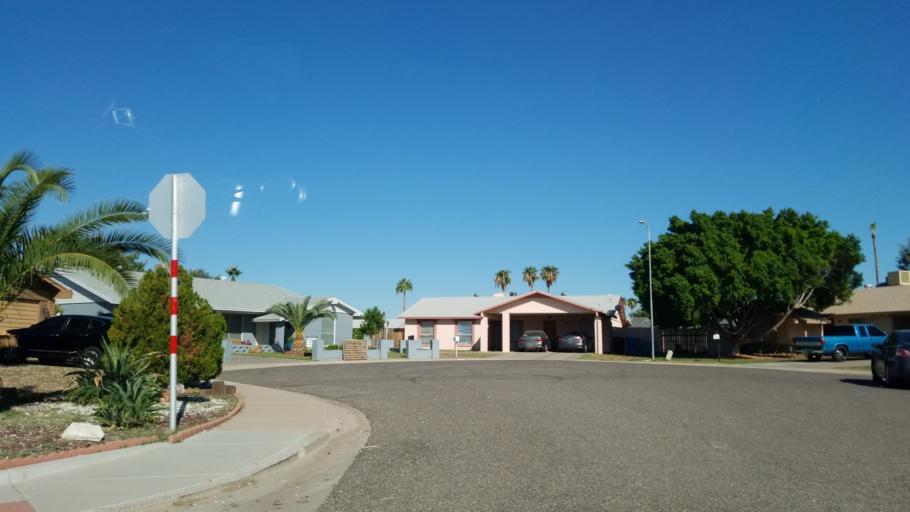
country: US
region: Arizona
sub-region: Maricopa County
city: Glendale
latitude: 33.5012
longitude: -112.2234
